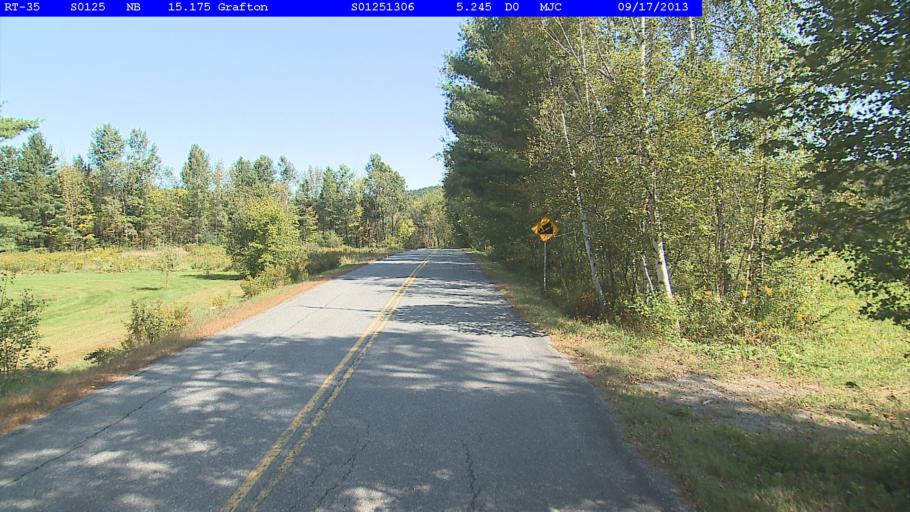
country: US
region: Vermont
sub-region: Windsor County
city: Chester
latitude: 43.1862
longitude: -72.5984
